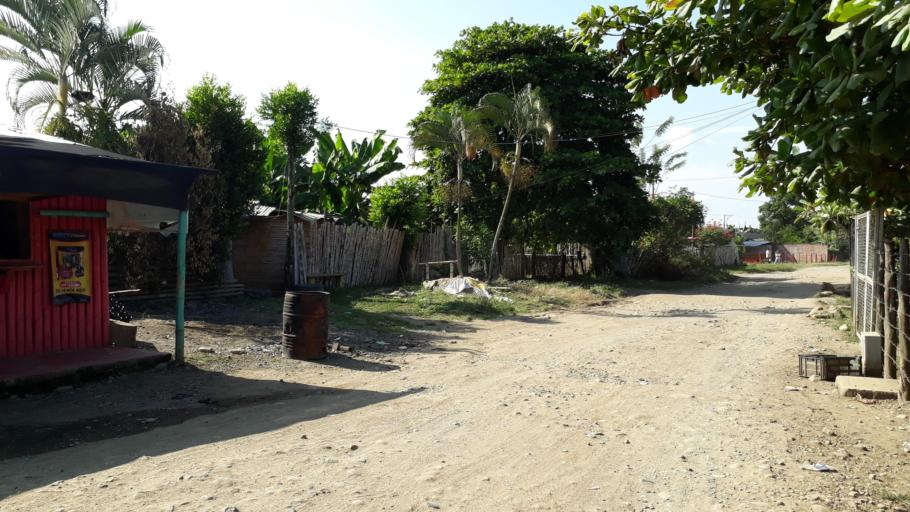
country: CO
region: Cauca
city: Buenos Aires
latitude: 3.1251
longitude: -76.6237
